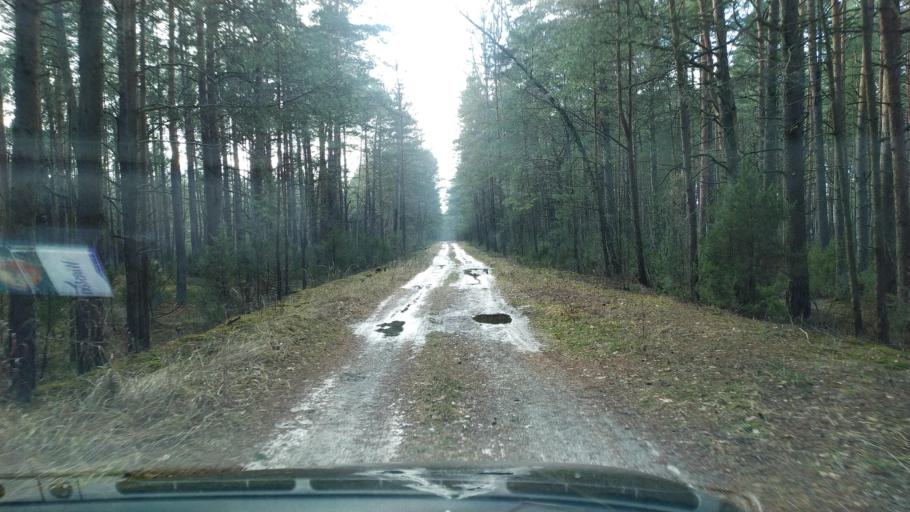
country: BY
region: Brest
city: Kamyanyets
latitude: 52.4287
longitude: 23.9977
